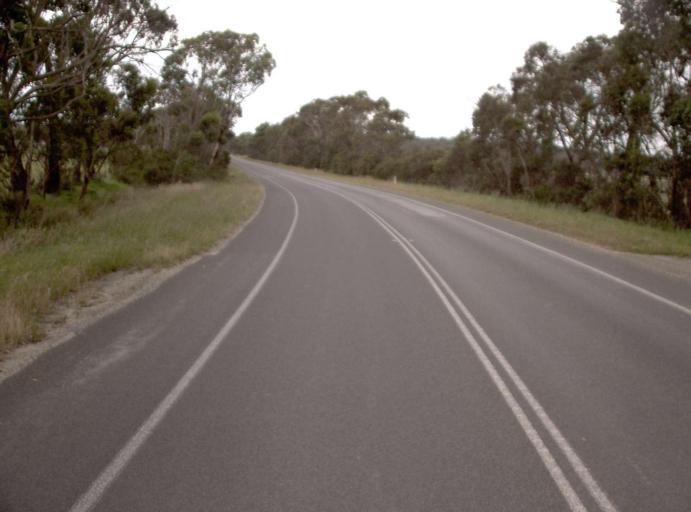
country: AU
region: Victoria
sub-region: Cardinia
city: Koo-Wee-Rup
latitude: -38.3300
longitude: 145.5941
